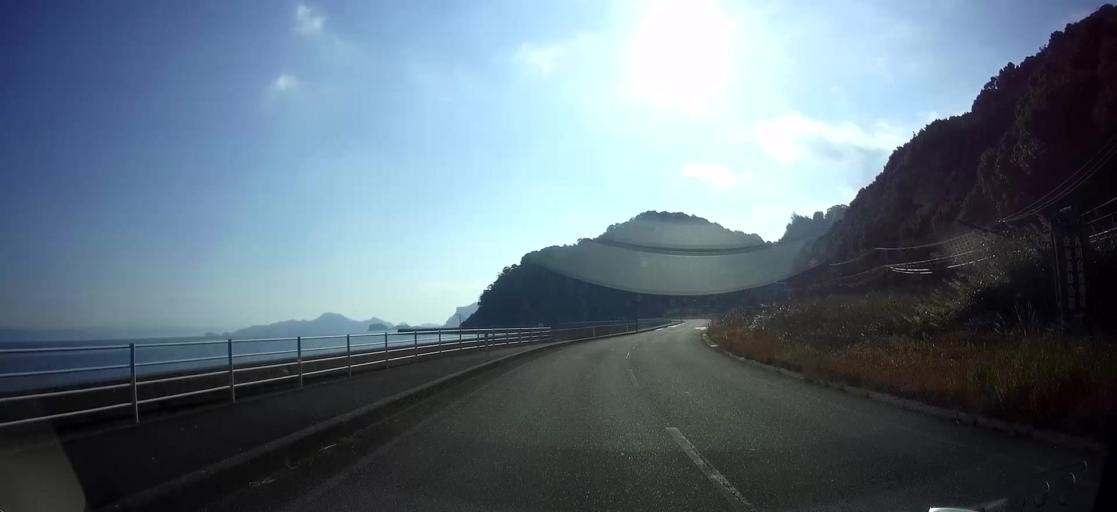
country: JP
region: Kumamoto
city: Yatsushiro
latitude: 32.4597
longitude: 130.4301
